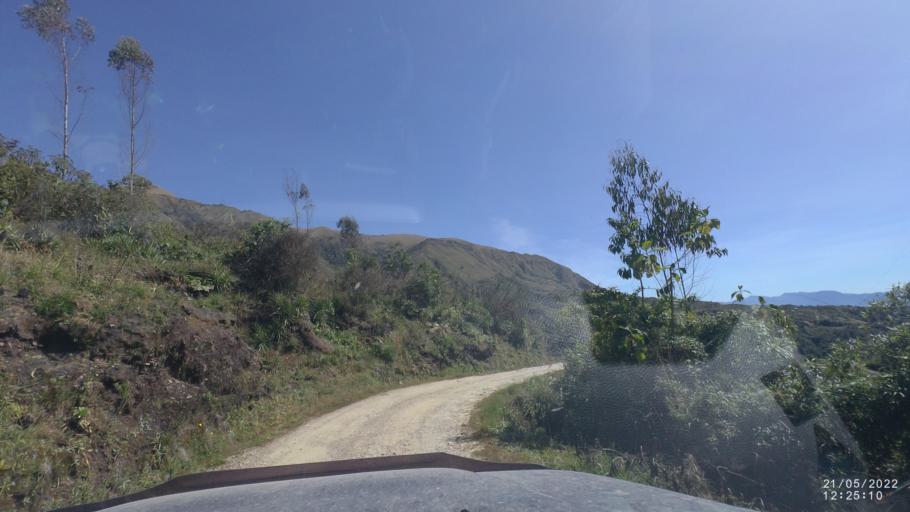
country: BO
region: Cochabamba
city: Colomi
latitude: -17.2193
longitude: -65.9073
